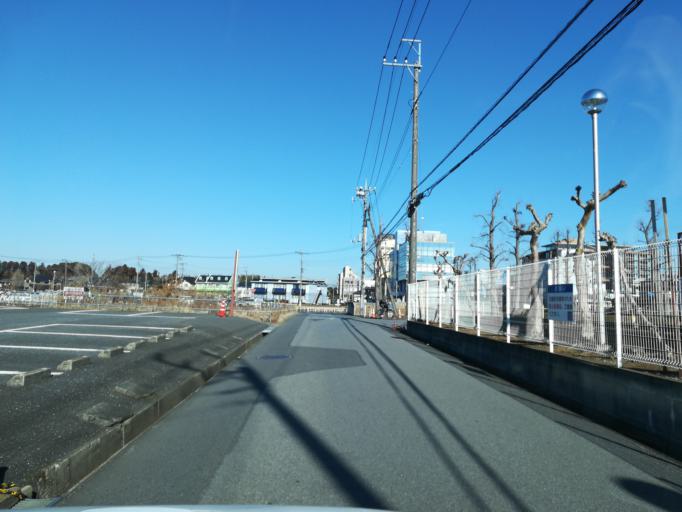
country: JP
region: Ibaraki
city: Naka
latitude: 36.0684
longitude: 140.1157
